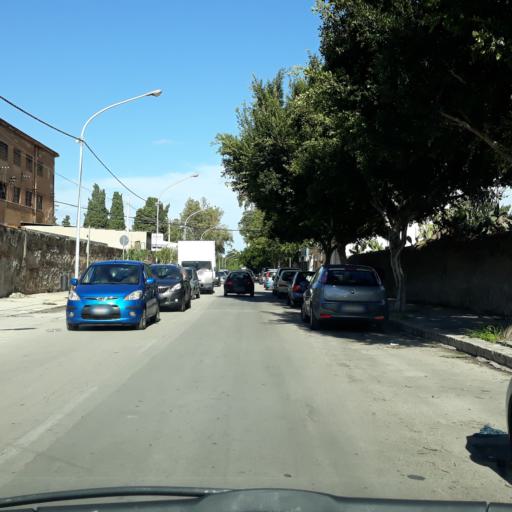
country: IT
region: Sicily
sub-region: Palermo
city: Palermo
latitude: 38.1557
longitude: 13.3706
